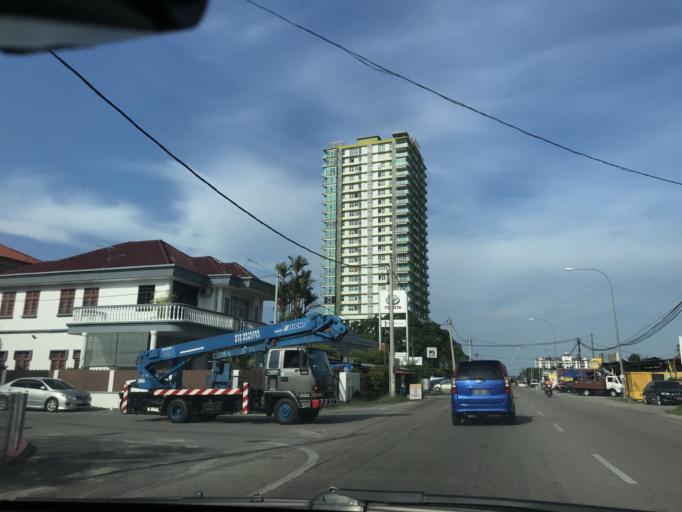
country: MY
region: Kelantan
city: Kota Bharu
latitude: 6.1243
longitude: 102.2676
